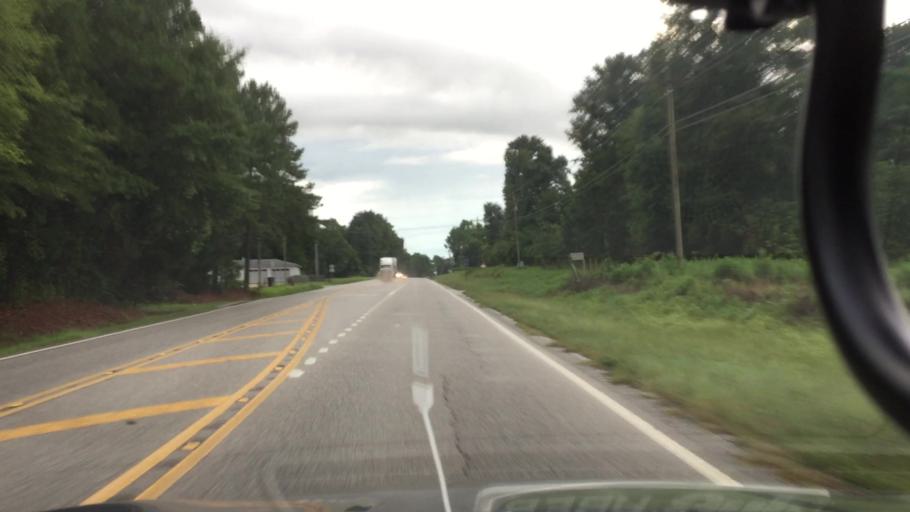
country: US
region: Alabama
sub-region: Pike County
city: Troy
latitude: 31.7321
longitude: -85.9576
